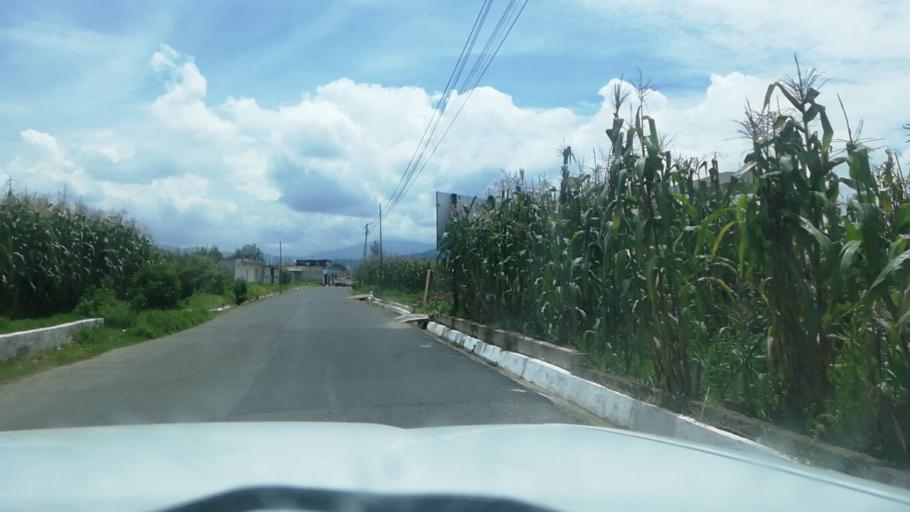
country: GT
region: Totonicapan
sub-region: Municipio de San Andres Xecul
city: San Andres Xecul
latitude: 14.9050
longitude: -91.4720
